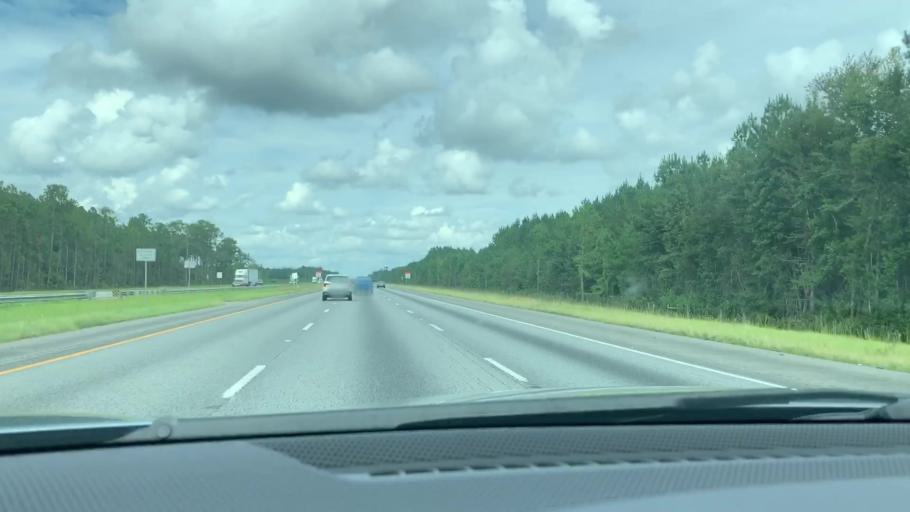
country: US
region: Georgia
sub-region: Liberty County
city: Midway
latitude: 31.6091
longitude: -81.4170
